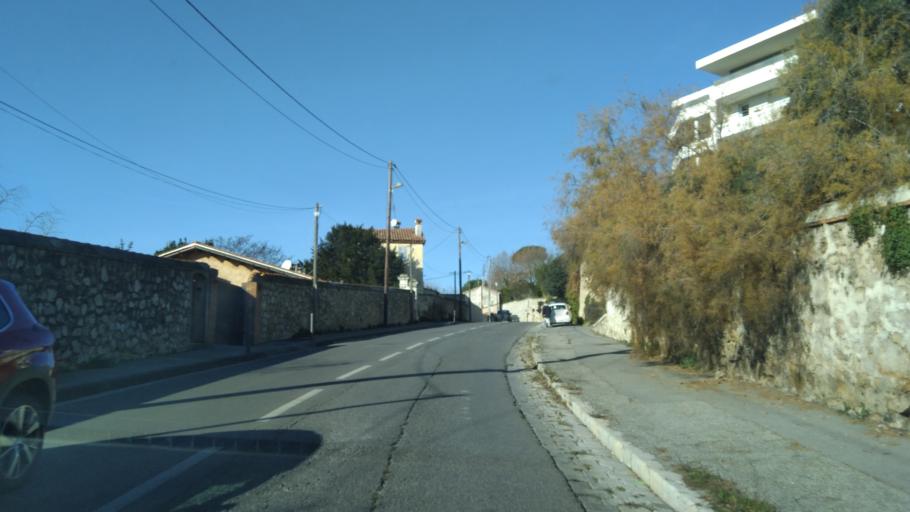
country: FR
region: Provence-Alpes-Cote d'Azur
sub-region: Departement des Bouches-du-Rhone
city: Marseille 12
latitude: 43.3024
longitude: 5.4437
